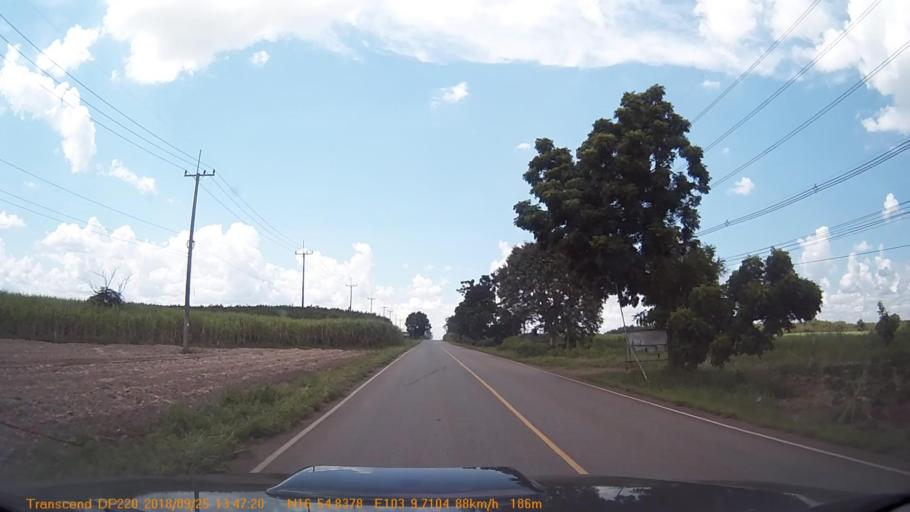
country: TH
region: Changwat Udon Thani
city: Si That
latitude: 16.9139
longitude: 103.1619
